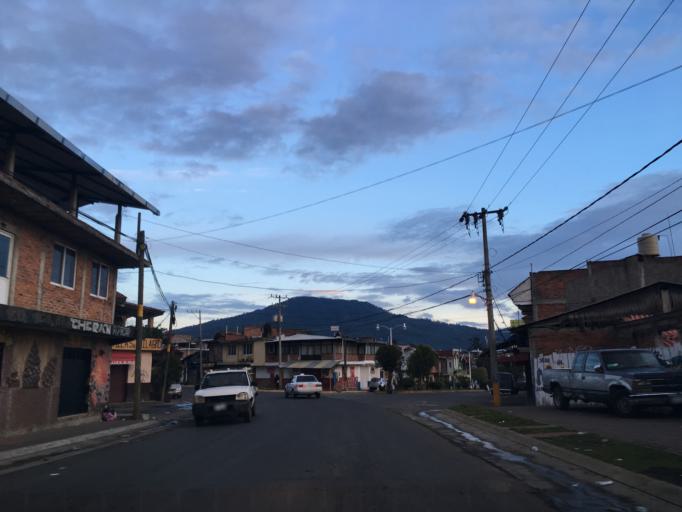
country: MX
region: Michoacan
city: Cheran
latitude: 19.6821
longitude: -101.9550
